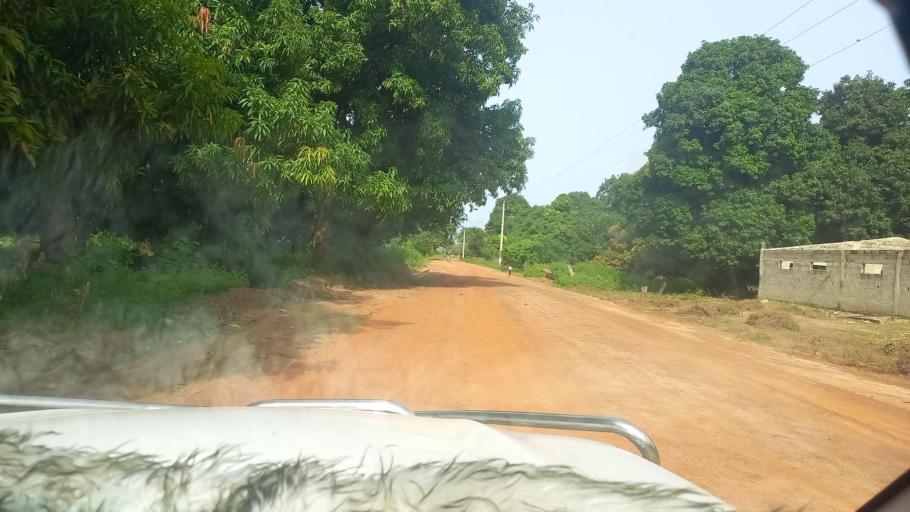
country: SN
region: Ziguinchor
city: Ziguinchor
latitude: 12.6703
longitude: -16.2740
